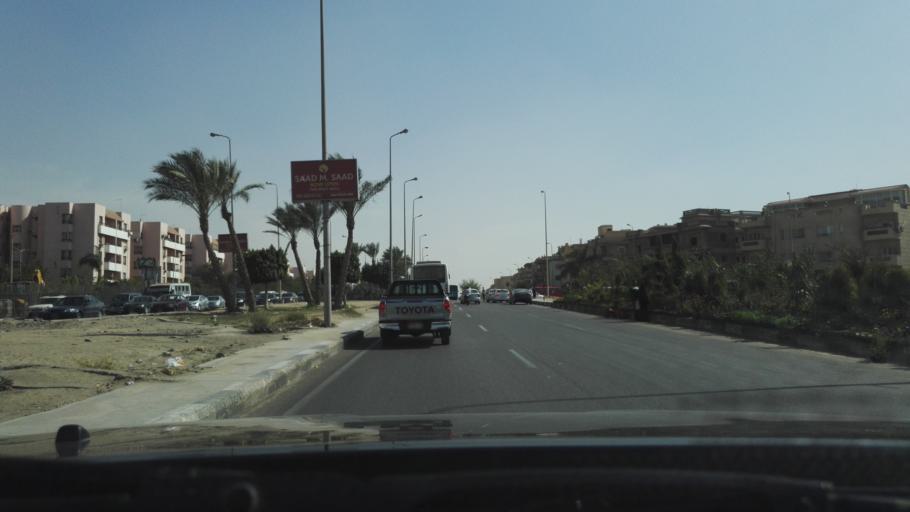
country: EG
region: Muhafazat al Qalyubiyah
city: Al Khankah
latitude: 30.0645
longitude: 31.4750
